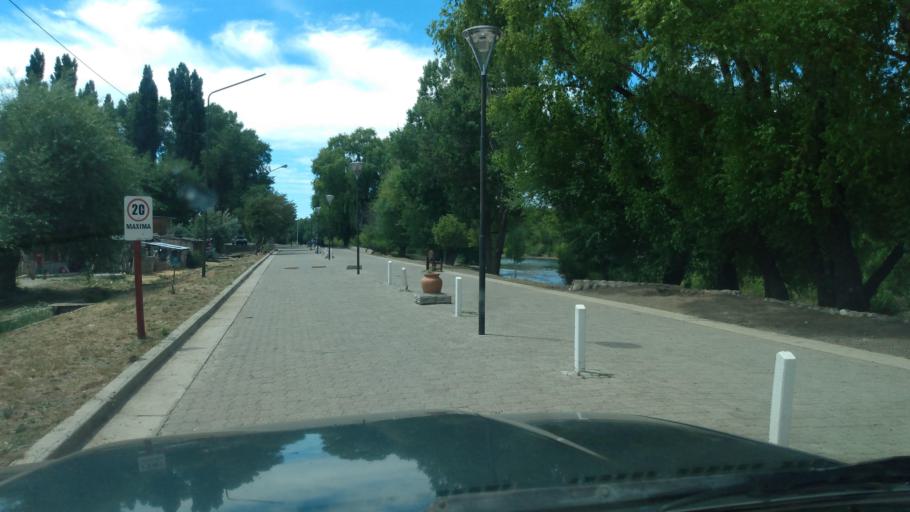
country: AR
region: Neuquen
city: Junin de los Andes
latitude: -39.9475
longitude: -71.0649
